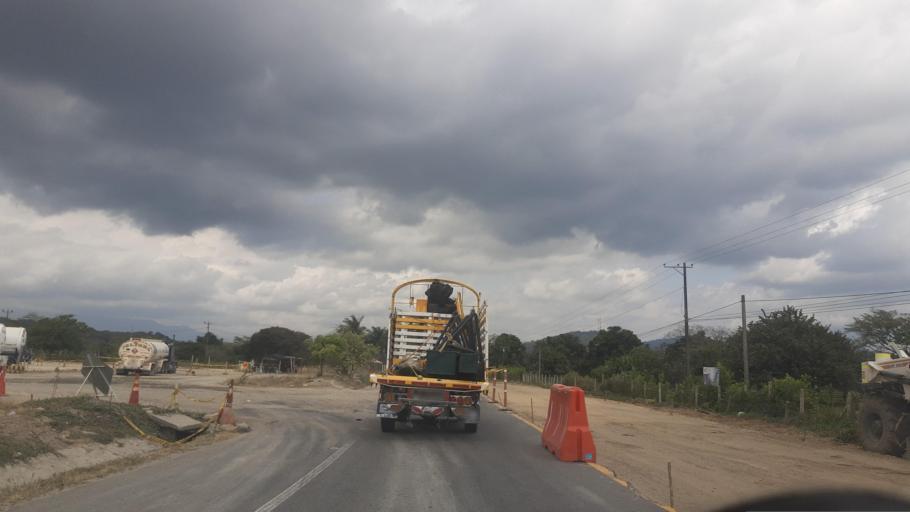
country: CO
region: Casanare
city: Tauramena
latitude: 4.9906
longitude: -72.6850
